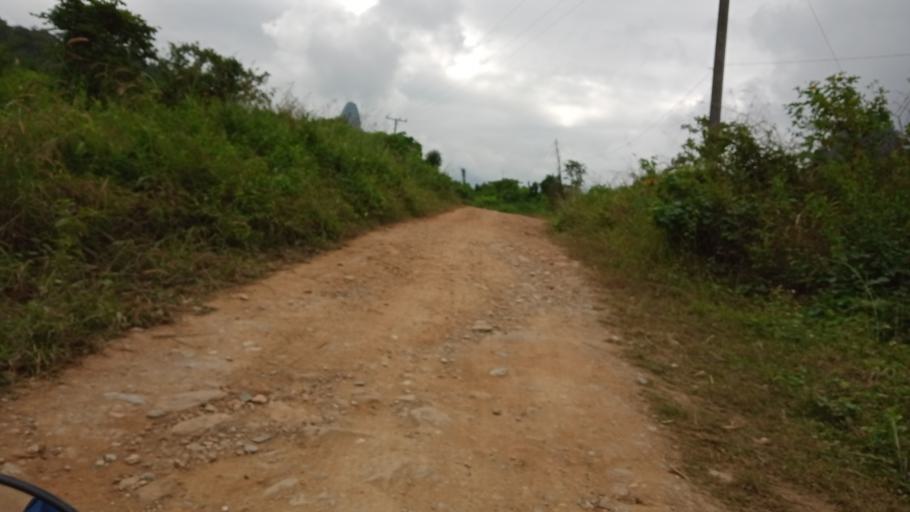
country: LA
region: Xiangkhoang
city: Phonsavan
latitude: 19.0871
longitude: 103.0078
